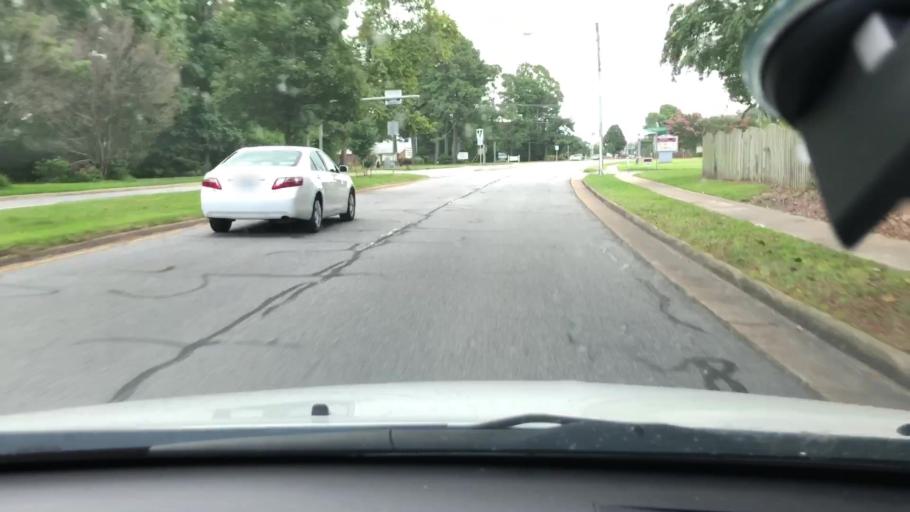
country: US
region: Virginia
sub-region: City of Chesapeake
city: Chesapeake
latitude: 36.8152
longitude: -76.1764
